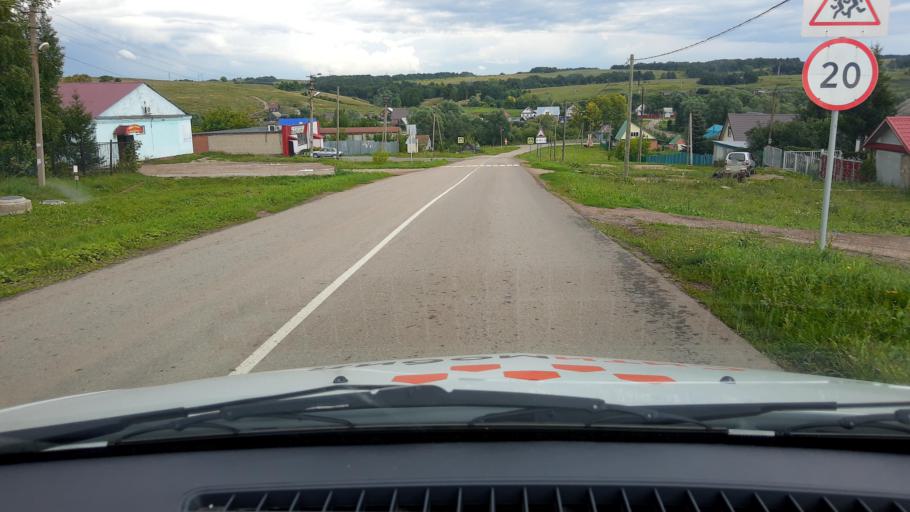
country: RU
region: Bashkortostan
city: Iglino
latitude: 54.9058
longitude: 56.1986
